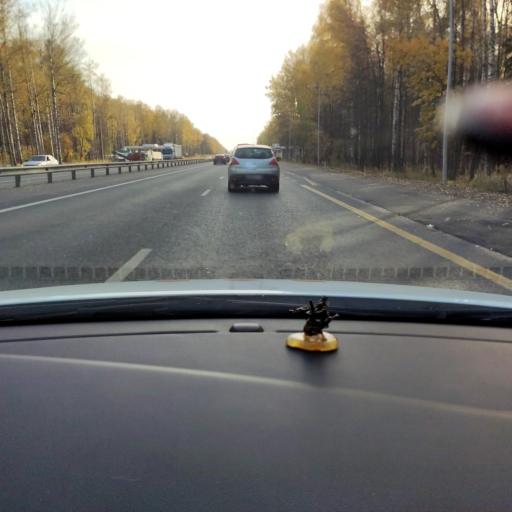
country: RU
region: Tatarstan
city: Osinovo
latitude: 55.8403
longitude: 48.8510
